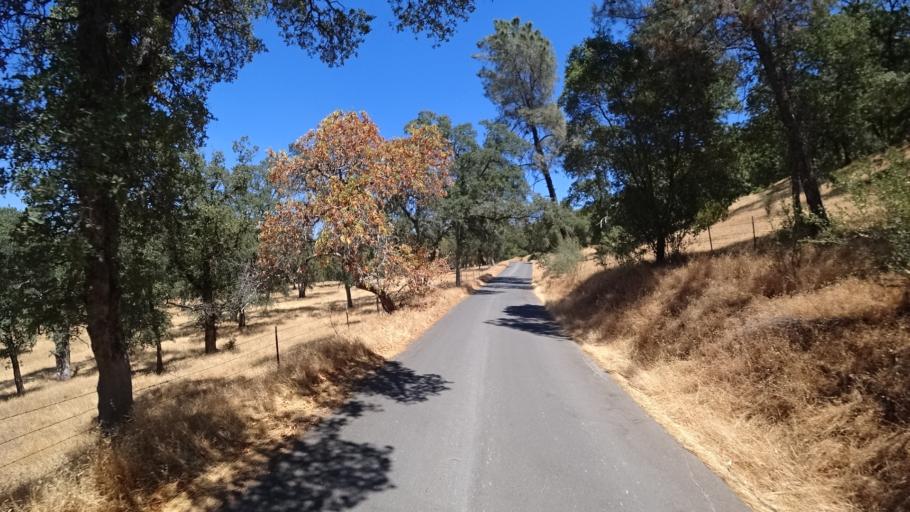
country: US
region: California
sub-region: Calaveras County
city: Murphys
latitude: 38.1152
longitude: -120.4729
